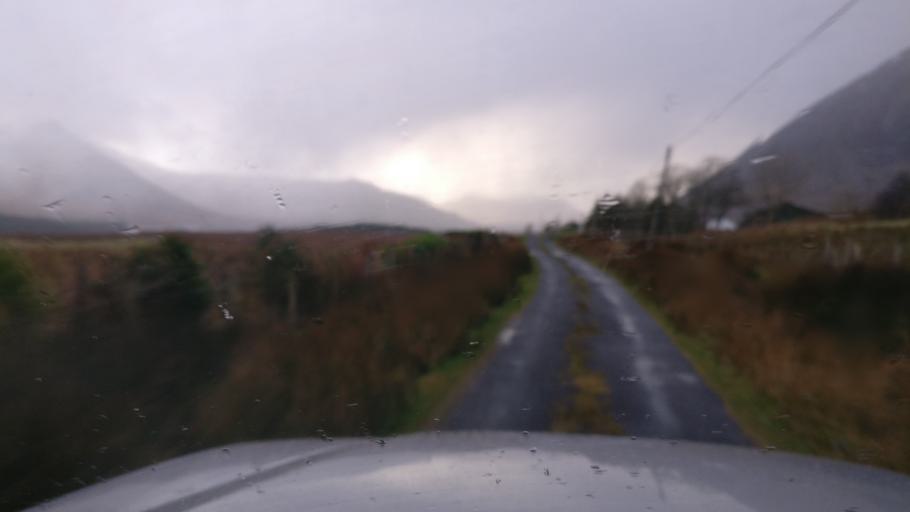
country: IE
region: Connaught
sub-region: County Galway
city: Clifden
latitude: 53.5129
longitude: -9.7116
